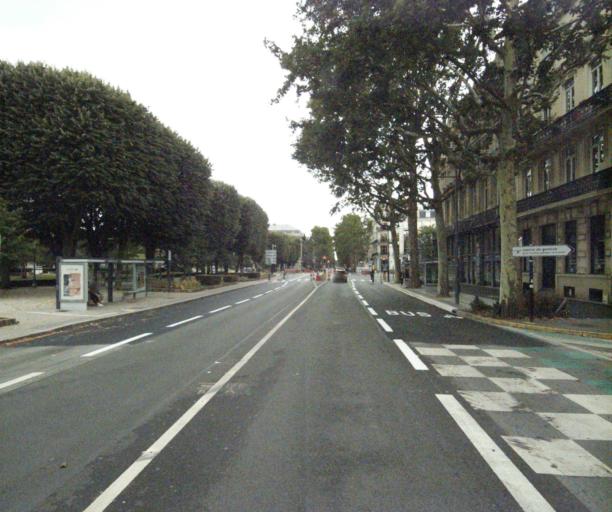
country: FR
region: Nord-Pas-de-Calais
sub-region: Departement du Nord
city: Lille
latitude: 50.6313
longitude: 3.0626
